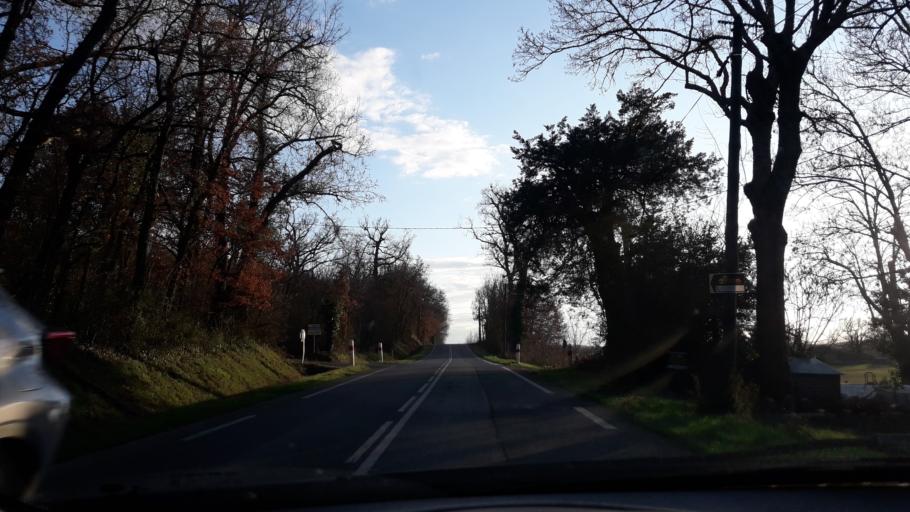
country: FR
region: Midi-Pyrenees
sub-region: Departement de la Haute-Garonne
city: Montaigut-sur-Save
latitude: 43.7099
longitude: 1.2457
